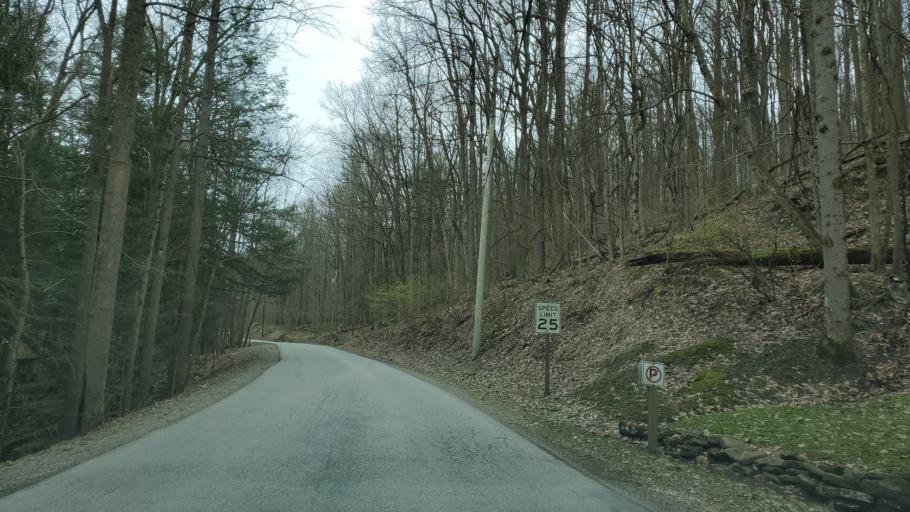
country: US
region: Pennsylvania
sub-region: Westmoreland County
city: Ligonier
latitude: 40.1715
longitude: -79.2361
